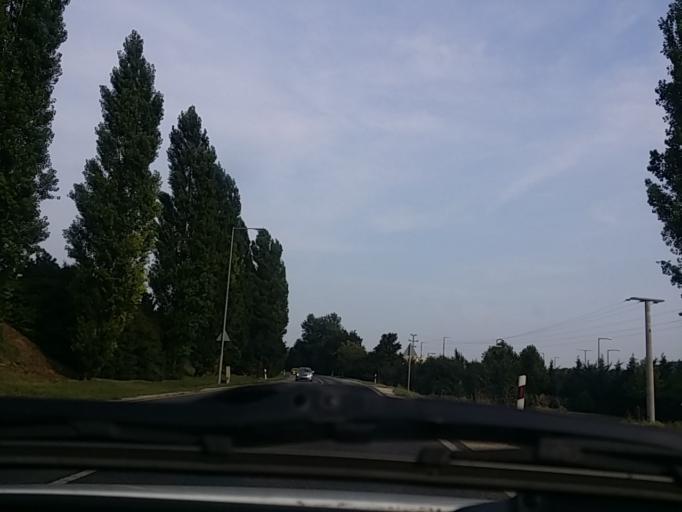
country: HU
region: Pest
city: Biatorbagy
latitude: 47.4743
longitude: 18.8450
